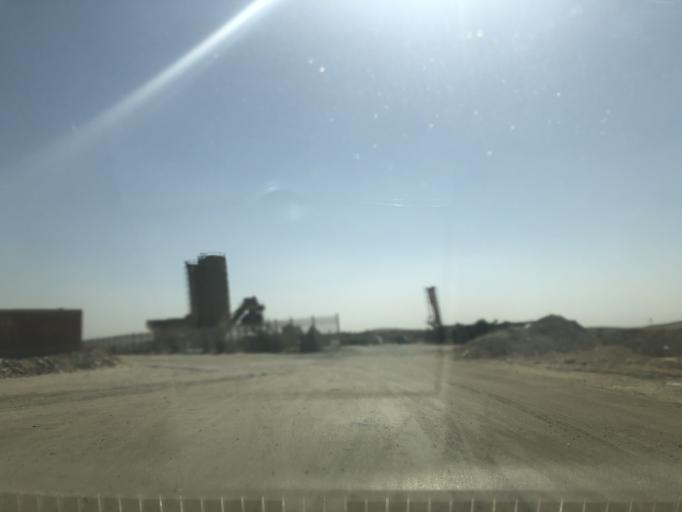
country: EG
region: Al Jizah
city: Madinat Sittah Uktubar
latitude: 29.9336
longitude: 30.9558
